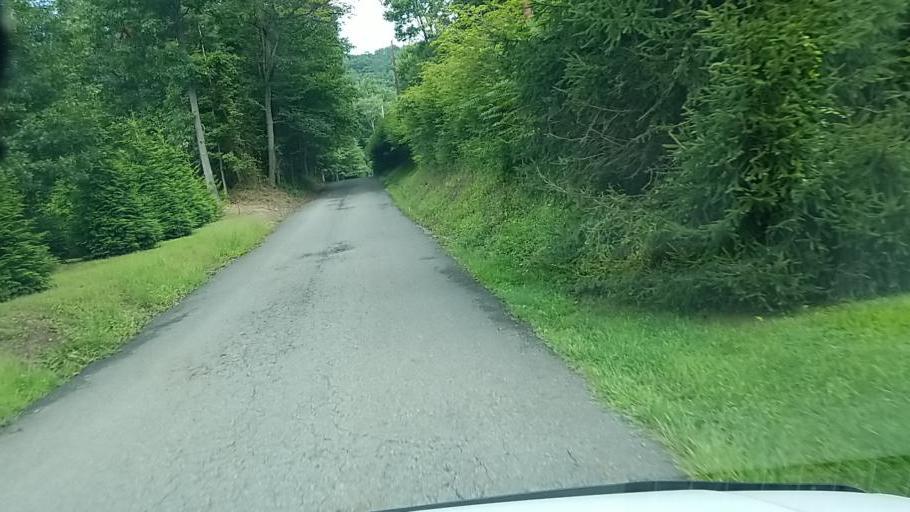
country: US
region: Pennsylvania
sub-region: Dauphin County
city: Millersburg
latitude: 40.5220
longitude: -76.9385
